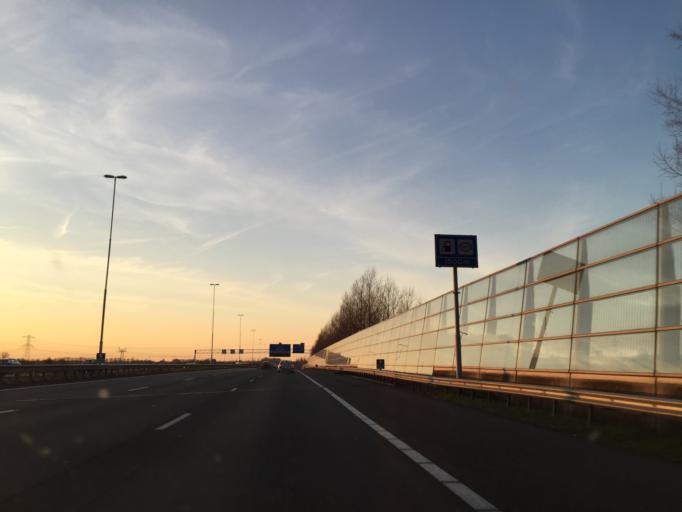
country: NL
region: North Brabant
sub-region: Gemeente Made en Drimmelen
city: Made
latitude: 51.6756
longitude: 4.6700
